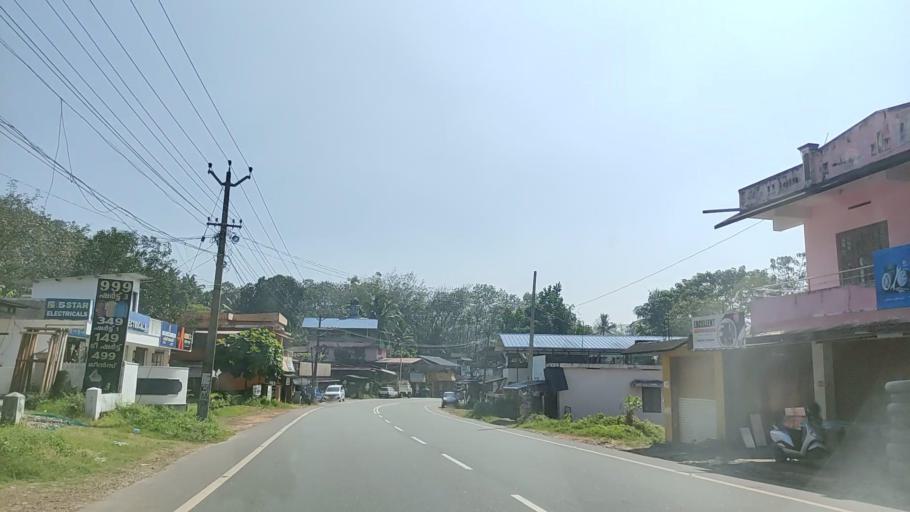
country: IN
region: Kerala
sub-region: Kollam
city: Punalur
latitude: 8.9154
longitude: 77.0443
